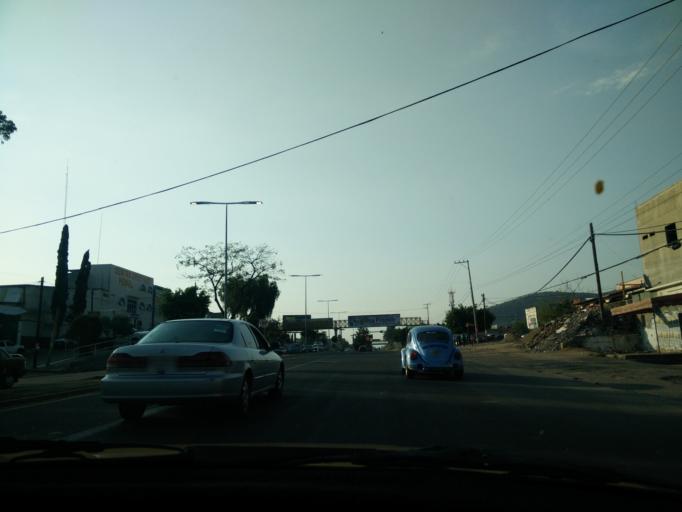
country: MX
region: Oaxaca
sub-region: Santa Maria Atzompa
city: San Jeronimo Yahuiche
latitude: 17.0924
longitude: -96.7477
